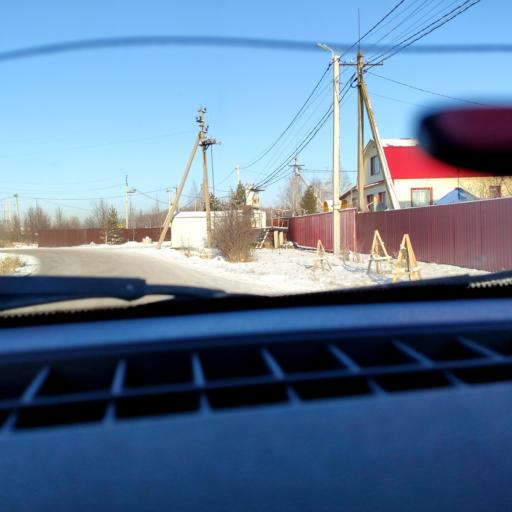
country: RU
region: Bashkortostan
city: Ufa
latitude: 54.6650
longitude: 55.9250
